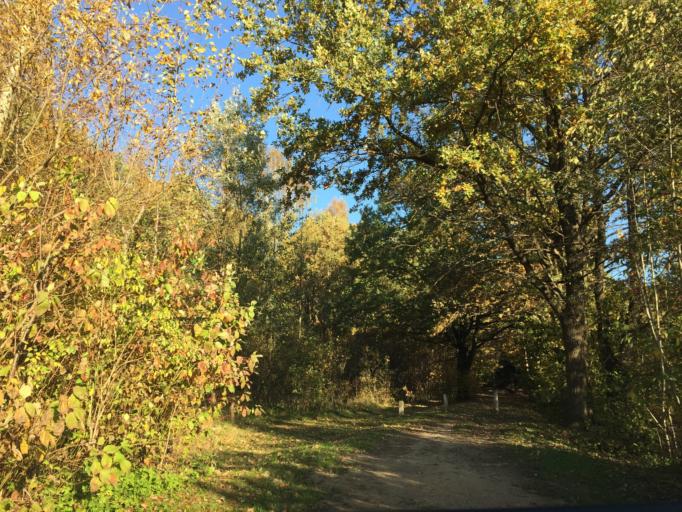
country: LT
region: Klaipedos apskritis
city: Kretinga
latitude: 55.8931
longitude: 21.2092
